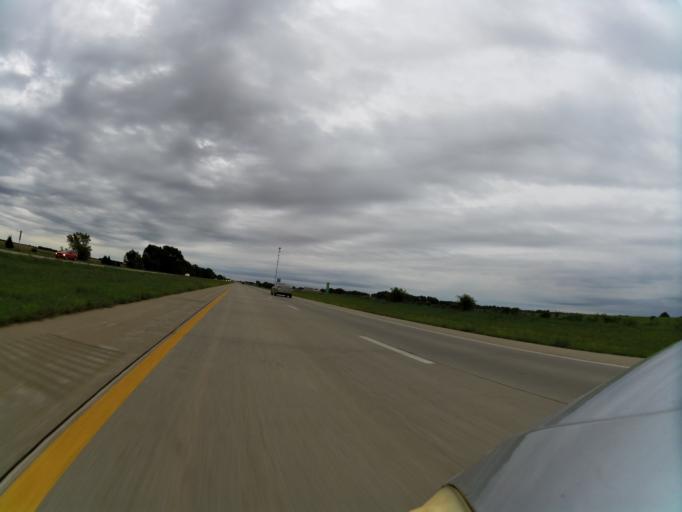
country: US
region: Kansas
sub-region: Reno County
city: Haven
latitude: 37.9145
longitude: -97.8184
